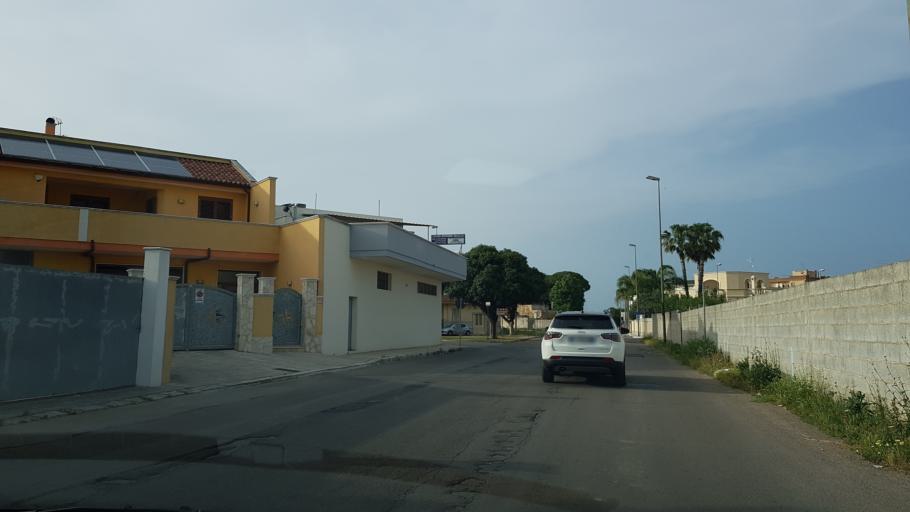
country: IT
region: Apulia
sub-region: Provincia di Brindisi
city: Cellino San Marco
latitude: 40.4724
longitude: 17.9707
